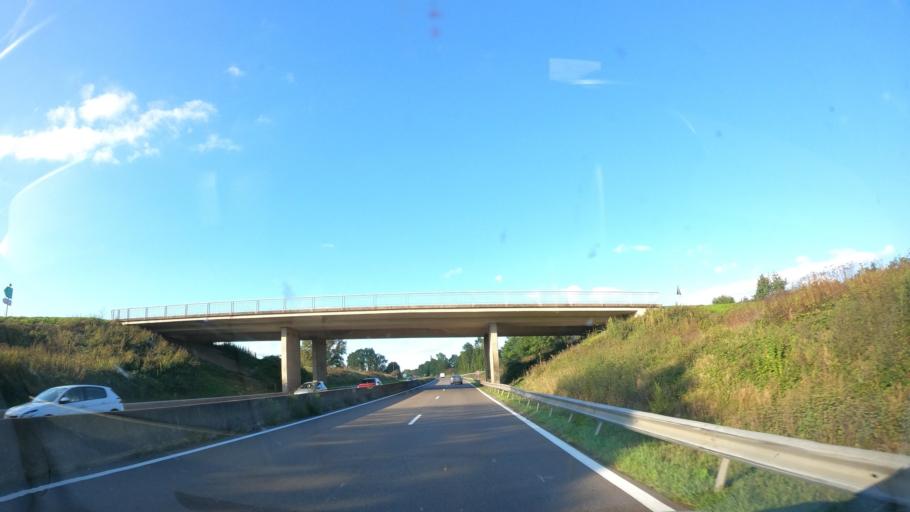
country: FR
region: Bourgogne
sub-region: Departement de Saone-et-Loire
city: Saint-Vallier
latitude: 46.6435
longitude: 4.3296
